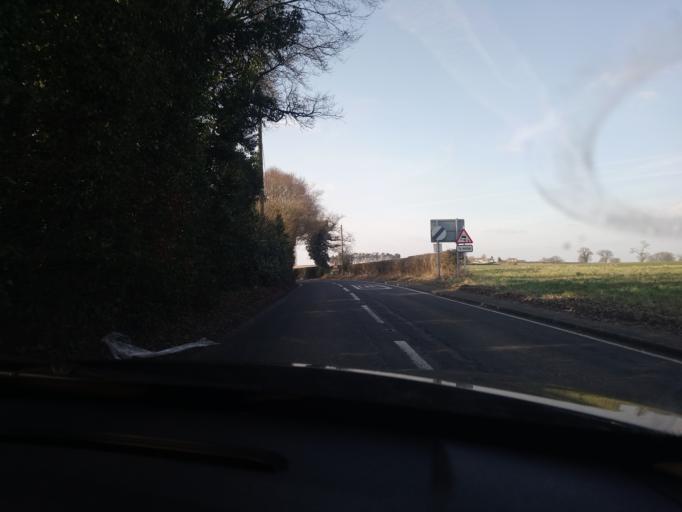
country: GB
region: England
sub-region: Shropshire
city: Clive
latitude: 52.7992
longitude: -2.7602
